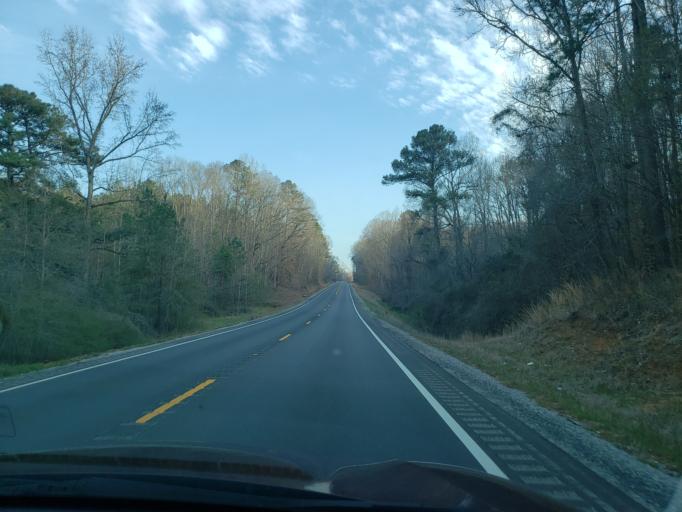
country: US
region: Alabama
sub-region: Hale County
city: Greensboro
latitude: 32.8148
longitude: -87.5972
